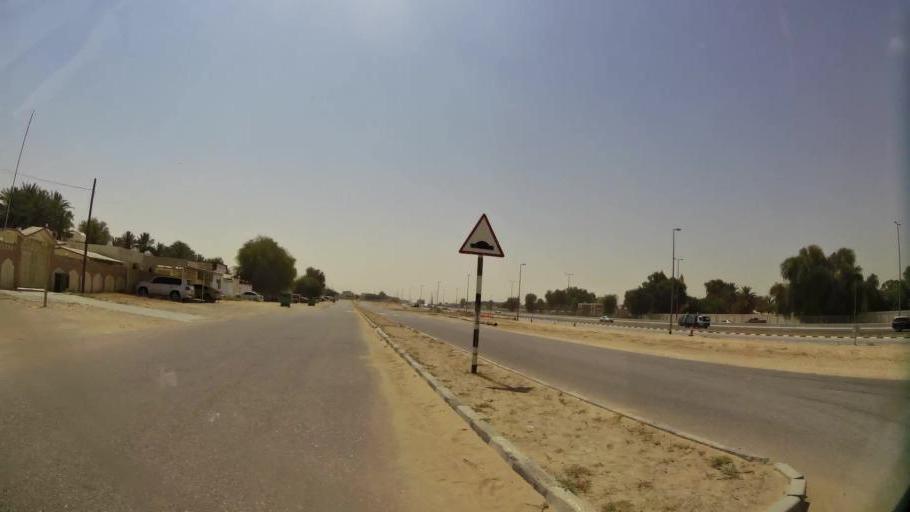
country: AE
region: Ajman
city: Ajman
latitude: 25.3951
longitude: 55.5300
